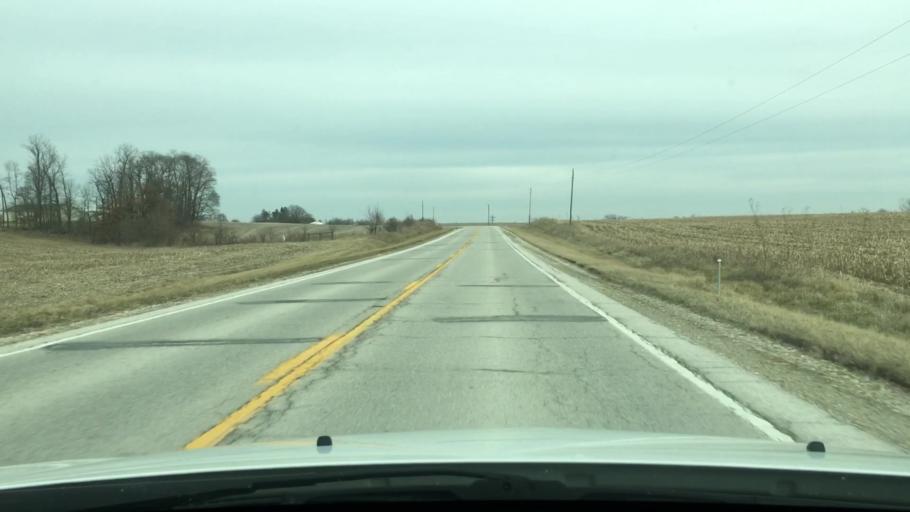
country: US
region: Illinois
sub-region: Pike County
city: Pittsfield
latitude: 39.5791
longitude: -90.9056
